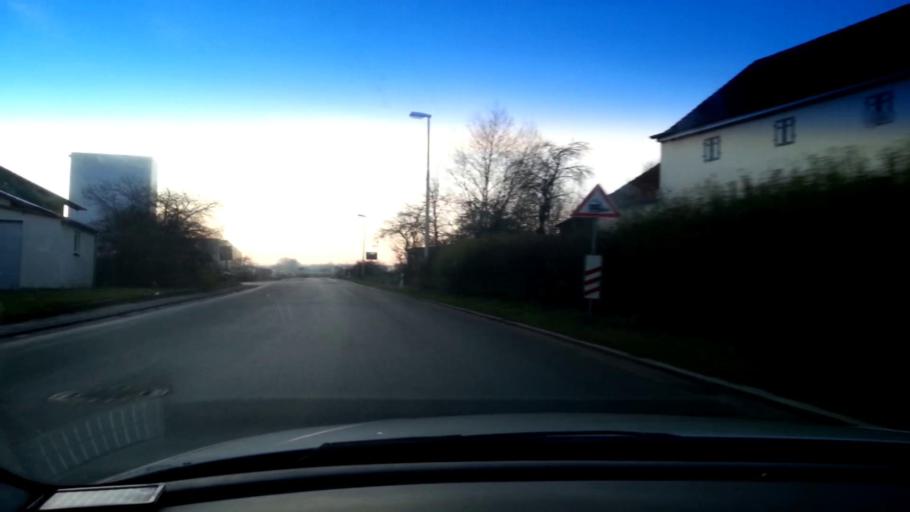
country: DE
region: Bavaria
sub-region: Upper Franconia
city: Pommersfelden
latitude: 49.7801
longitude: 10.8375
